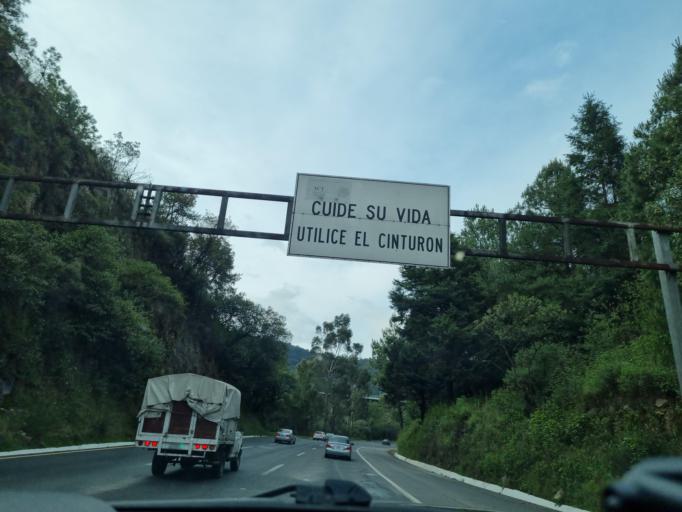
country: MX
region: Morelos
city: San Jeronimo Acazulco
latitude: 19.2939
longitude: -99.4173
